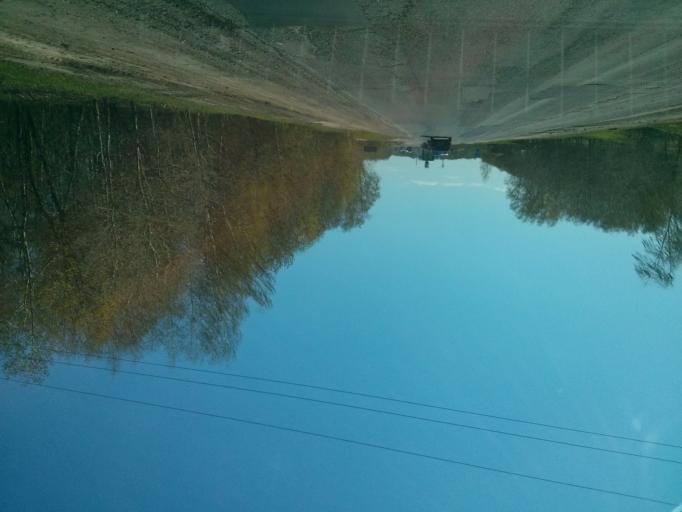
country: RU
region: Nizjnij Novgorod
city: Afonino
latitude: 56.2157
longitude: 44.0362
